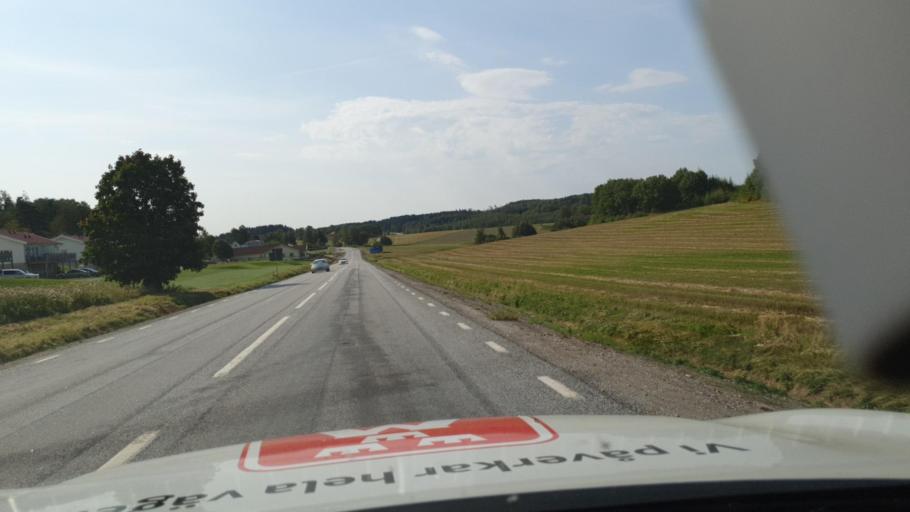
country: SE
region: Vaestra Goetaland
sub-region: Tanums Kommun
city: Tanumshede
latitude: 58.7752
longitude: 11.5590
